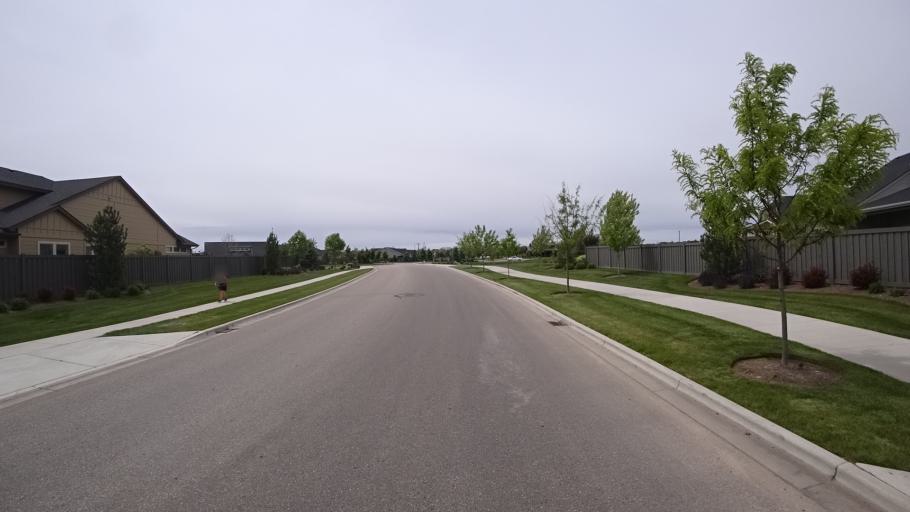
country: US
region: Idaho
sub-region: Ada County
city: Meridian
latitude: 43.5543
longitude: -116.3519
